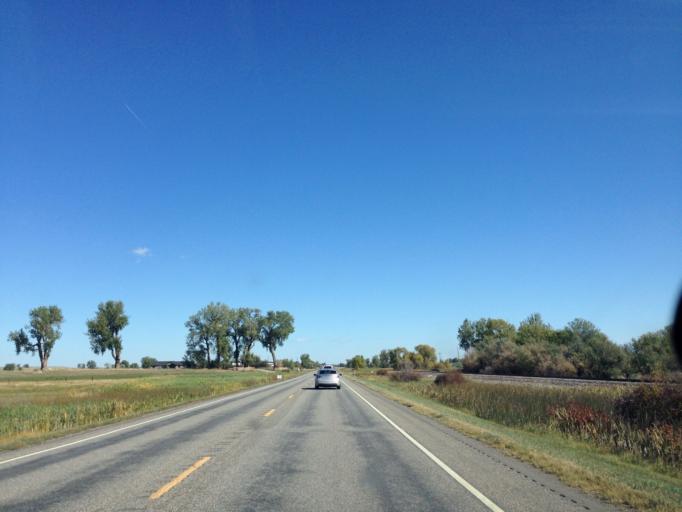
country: US
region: Montana
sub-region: Yellowstone County
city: Laurel
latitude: 45.6012
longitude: -108.8054
